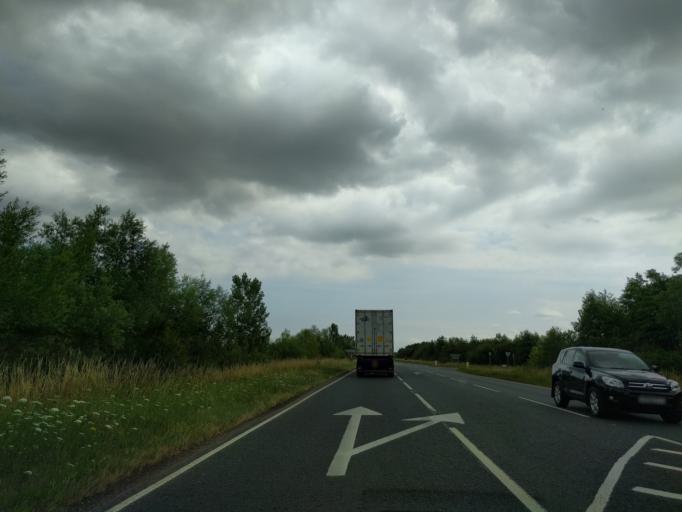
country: GB
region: England
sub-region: Cambridgeshire
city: Needingworth
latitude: 52.3387
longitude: -0.0231
